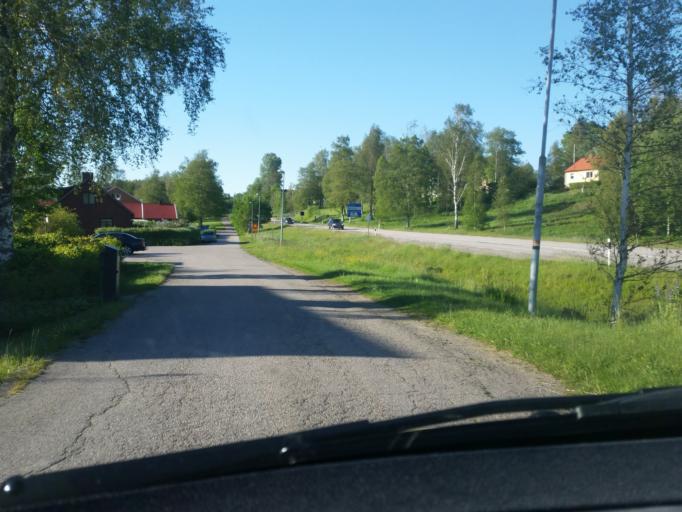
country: SE
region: Vaestra Goetaland
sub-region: Fargelanda Kommun
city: Faergelanda
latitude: 58.5684
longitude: 12.0041
